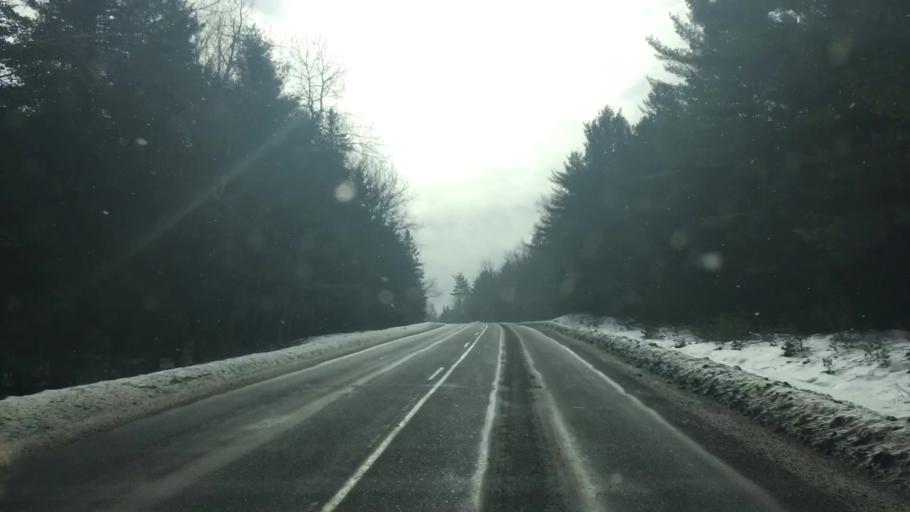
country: US
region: Maine
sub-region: Washington County
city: Calais
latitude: 45.0685
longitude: -67.3310
